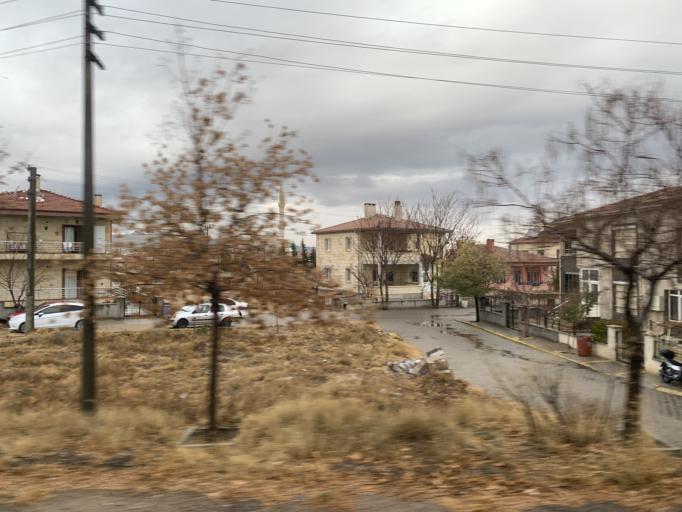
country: TR
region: Nevsehir
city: Avanos
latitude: 38.7079
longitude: 34.8578
